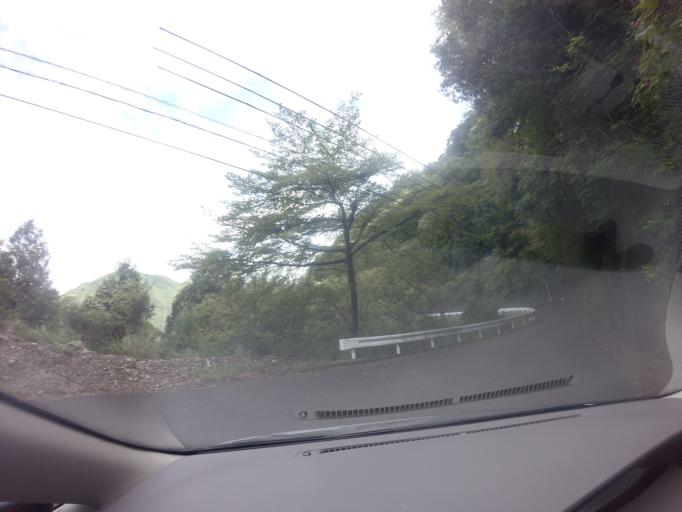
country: JP
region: Wakayama
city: Shingu
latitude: 33.9653
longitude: 135.8514
